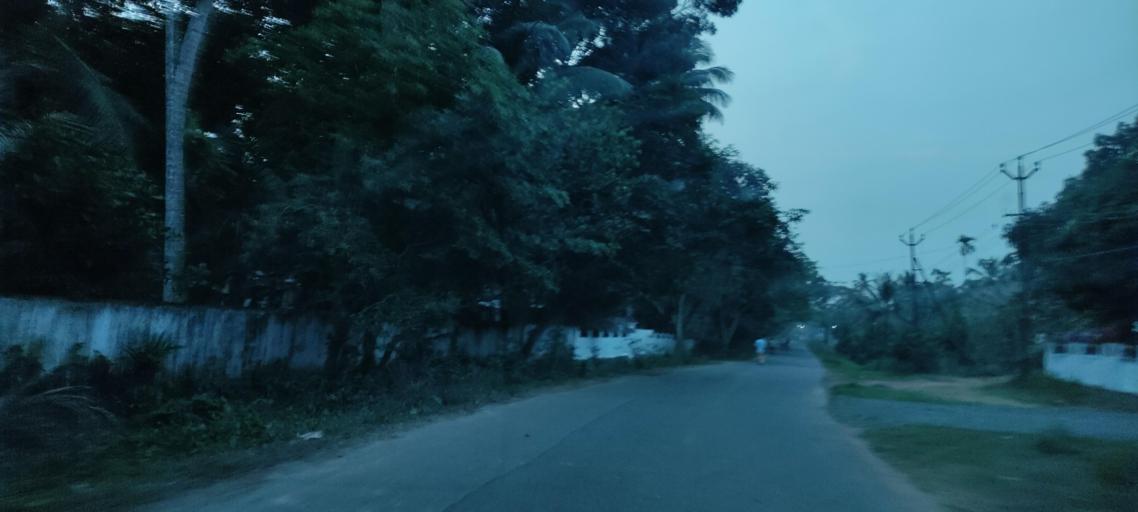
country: IN
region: Kerala
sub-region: Alappuzha
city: Mavelikara
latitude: 9.3299
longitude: 76.4800
